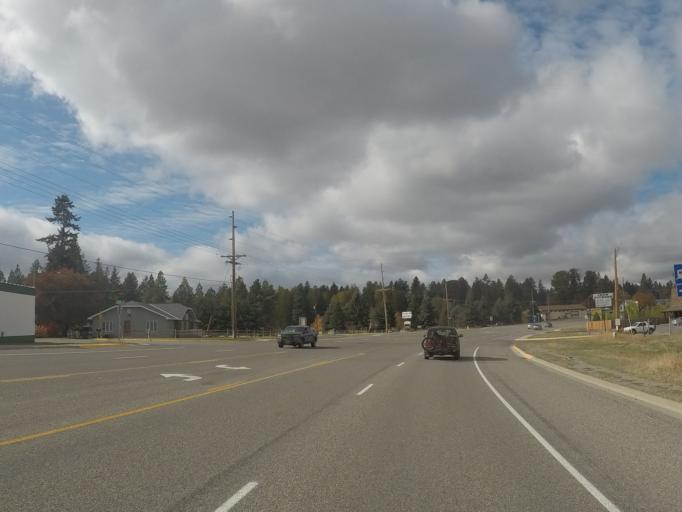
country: US
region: Montana
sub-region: Flathead County
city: Columbia Falls
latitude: 48.3670
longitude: -114.1743
